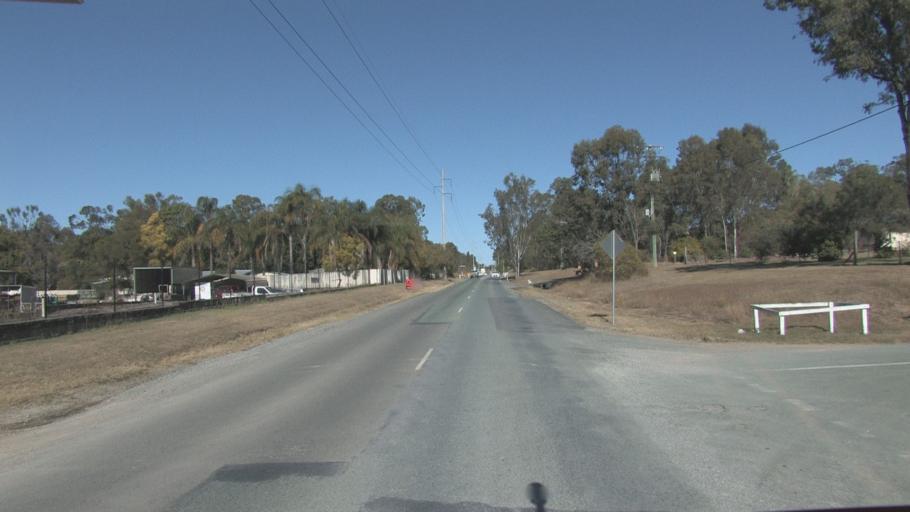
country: AU
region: Queensland
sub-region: Logan
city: Cedar Vale
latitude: -27.8497
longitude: 153.0211
